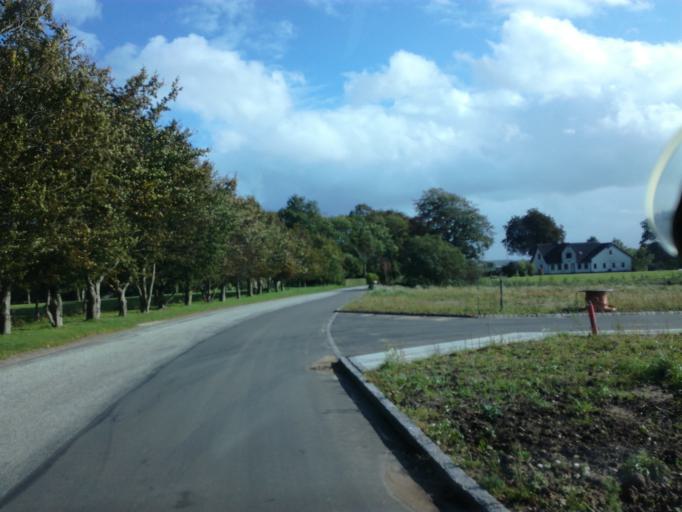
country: DK
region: South Denmark
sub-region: Vejle Kommune
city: Brejning
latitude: 55.6372
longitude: 9.7129
